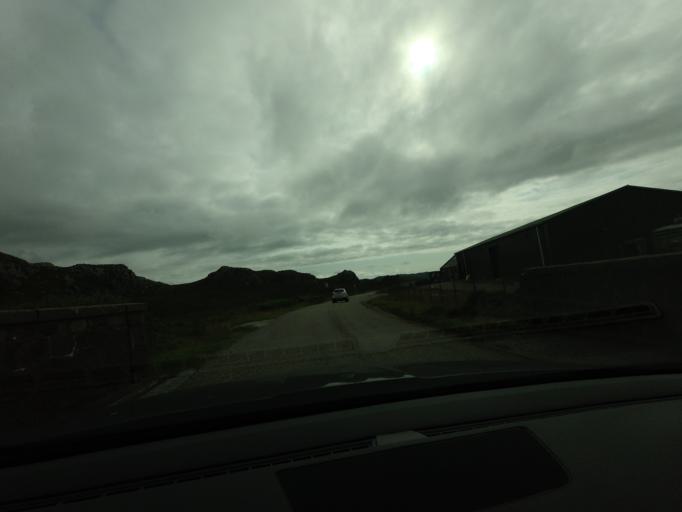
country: GB
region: Scotland
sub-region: Highland
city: Ullapool
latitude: 58.4302
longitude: -4.9720
